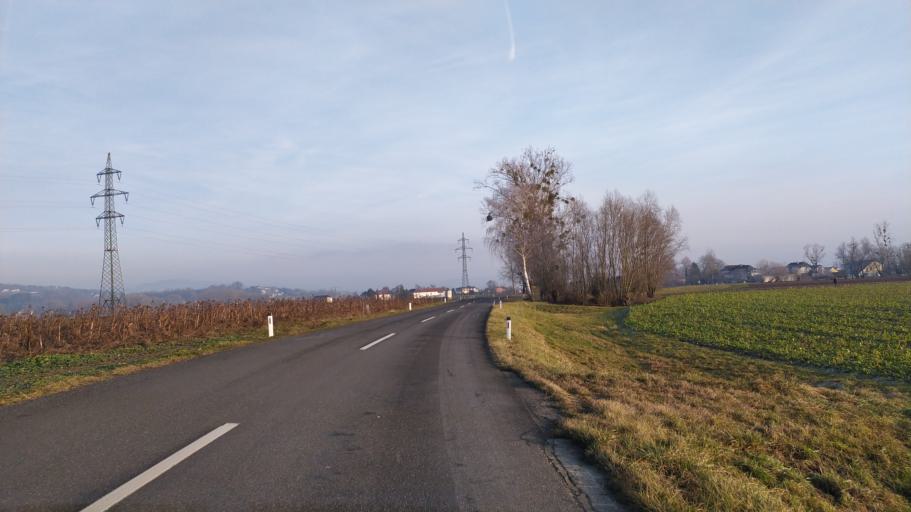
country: AT
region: Upper Austria
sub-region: Politischer Bezirk Urfahr-Umgebung
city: Goldworth
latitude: 48.3395
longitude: 14.0898
